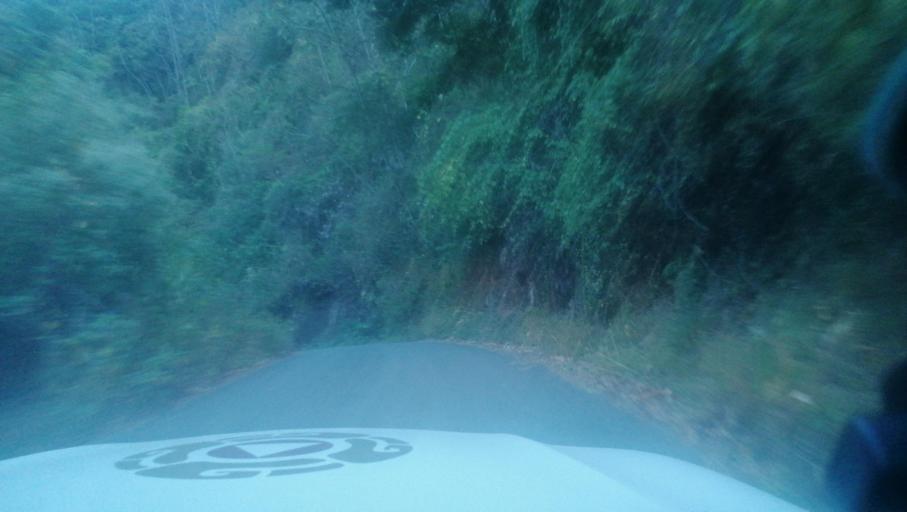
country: MX
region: Chiapas
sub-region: Cacahoatan
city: Benito Juarez
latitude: 15.1288
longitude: -92.2078
